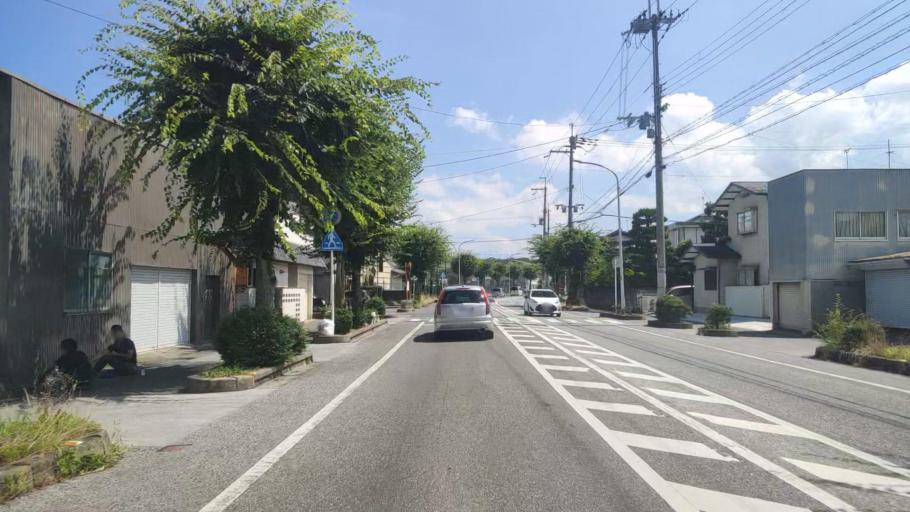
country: JP
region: Shiga Prefecture
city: Hikone
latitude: 35.2692
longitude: 136.2471
